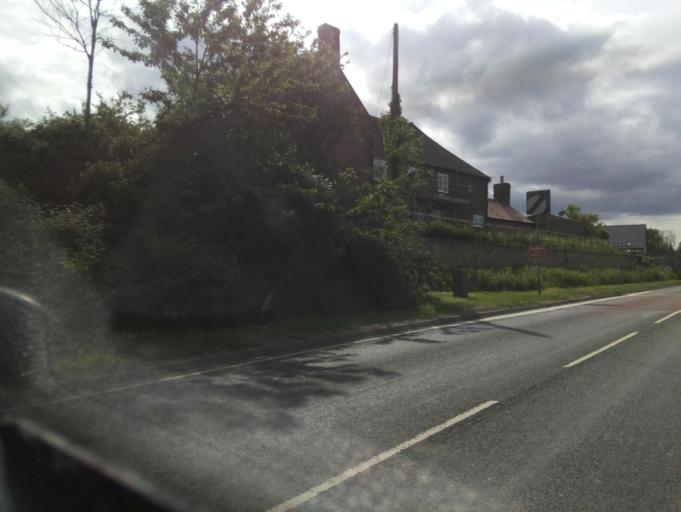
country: GB
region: England
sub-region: Worcestershire
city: Pershore
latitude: 52.1155
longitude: -2.0904
